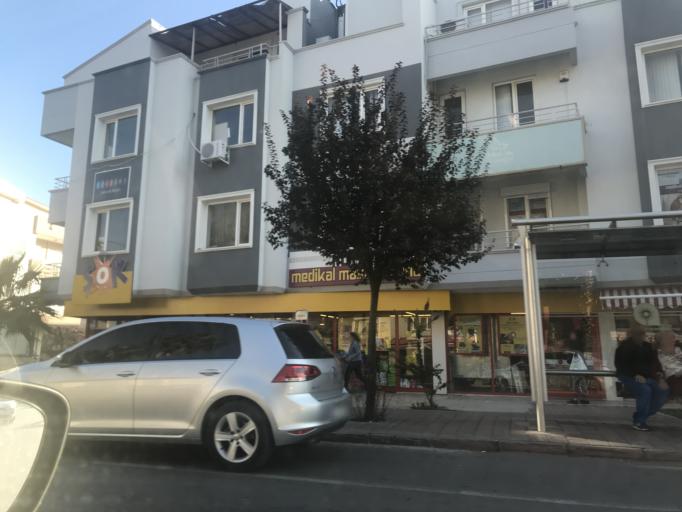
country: TR
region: Antalya
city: Antalya
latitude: 36.8550
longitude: 30.7796
